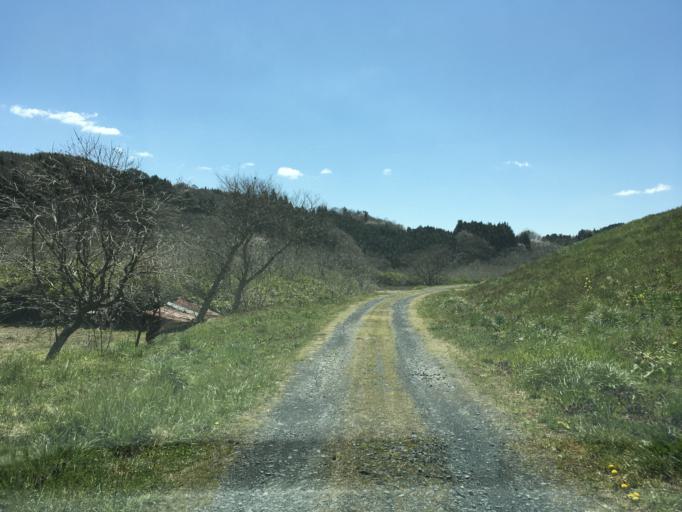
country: JP
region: Iwate
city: Ichinoseki
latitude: 38.8323
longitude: 141.2591
